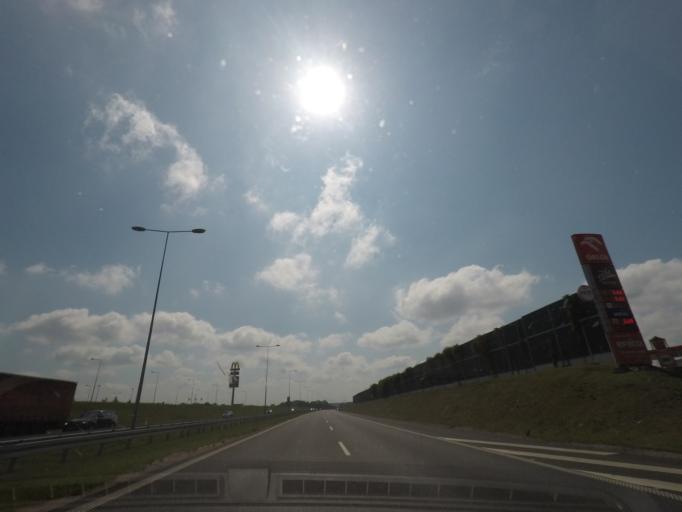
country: PL
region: Kujawsko-Pomorskie
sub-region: Powiat wloclawski
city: Brzesc Kujawski
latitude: 52.6562
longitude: 18.9287
